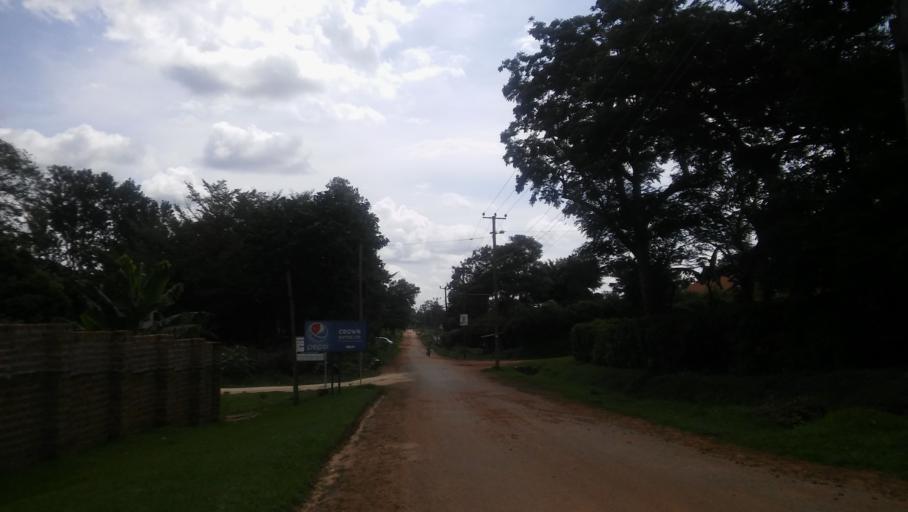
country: UG
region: Eastern Region
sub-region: Mbale District
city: Mbale
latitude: 1.0688
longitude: 34.1974
